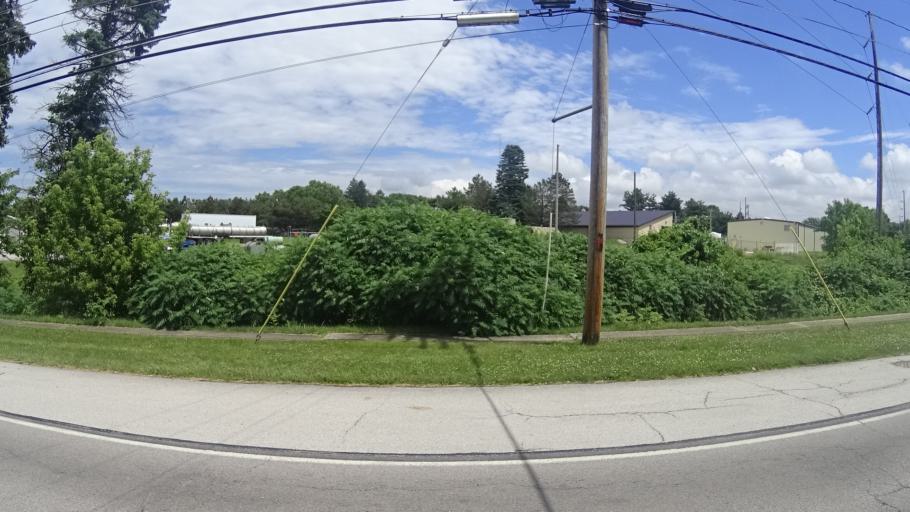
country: US
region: Ohio
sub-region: Erie County
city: Milan
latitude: 41.2919
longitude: -82.6043
